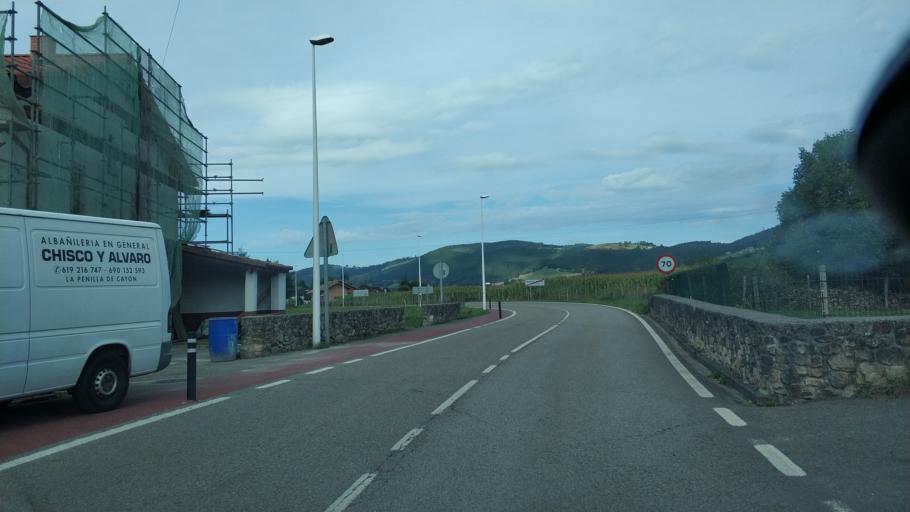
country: ES
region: Cantabria
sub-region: Provincia de Cantabria
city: Santa Maria de Cayon
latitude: 43.3086
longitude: -3.8618
